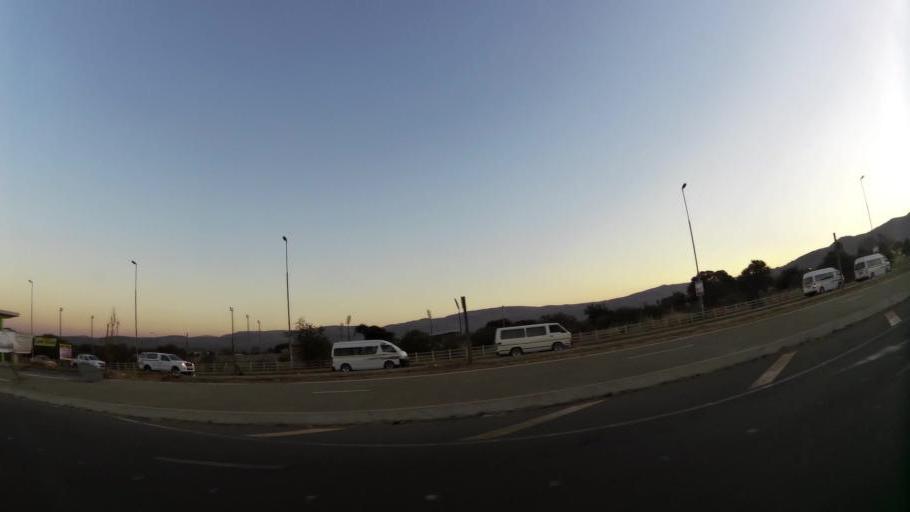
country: ZA
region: North-West
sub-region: Bojanala Platinum District Municipality
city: Rustenburg
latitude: -25.6575
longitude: 27.2249
